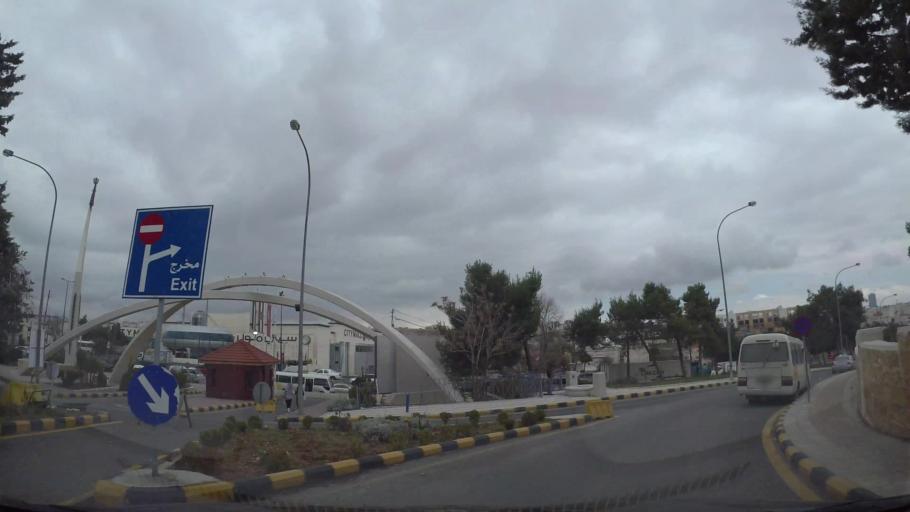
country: JO
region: Amman
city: Wadi as Sir
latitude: 31.9787
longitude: 35.8358
